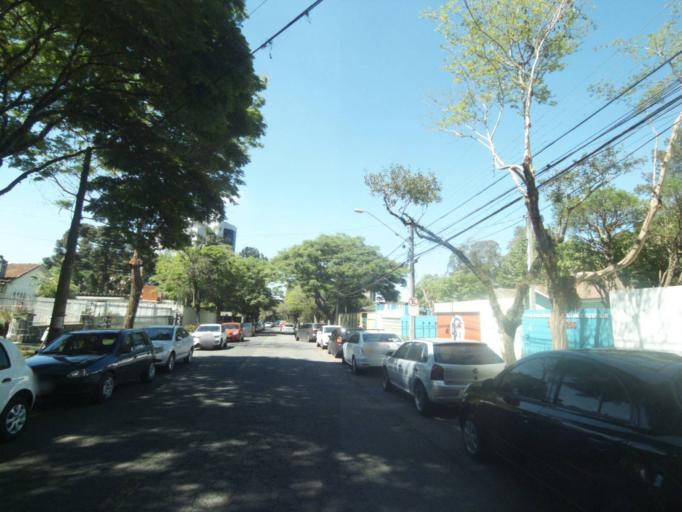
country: BR
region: Parana
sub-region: Curitiba
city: Curitiba
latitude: -25.4102
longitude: -49.2512
